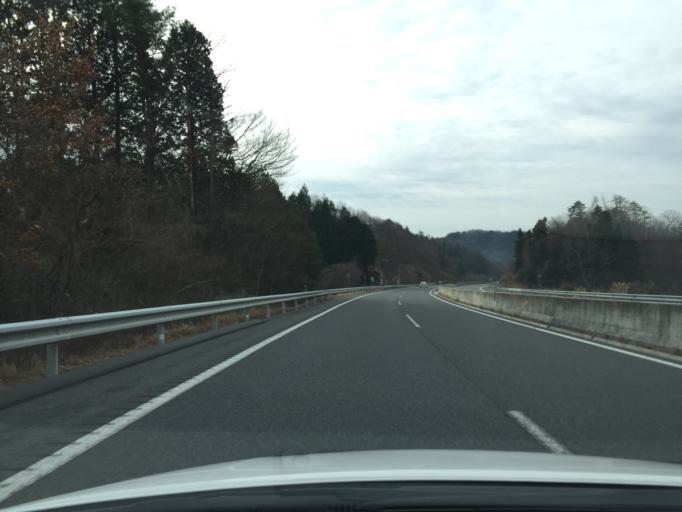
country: JP
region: Fukushima
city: Funehikimachi-funehiki
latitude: 37.3218
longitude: 140.6164
